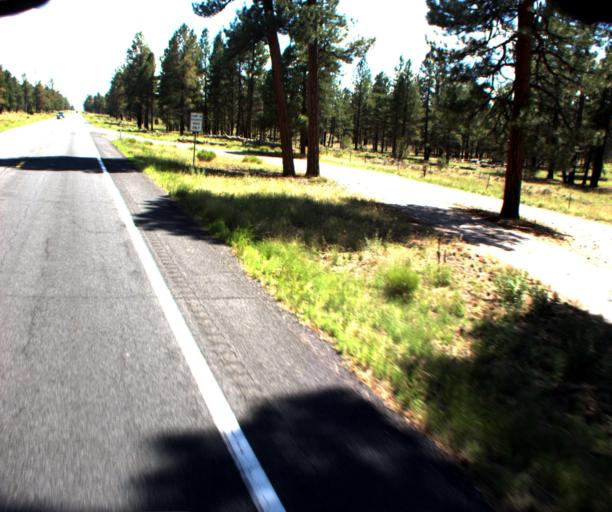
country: US
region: Arizona
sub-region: Coconino County
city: Grand Canyon Village
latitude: 35.9184
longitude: -112.1301
